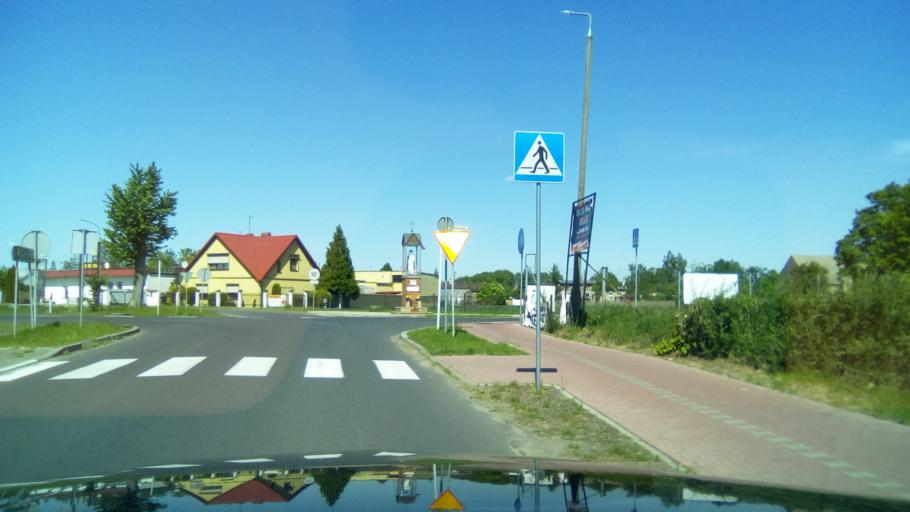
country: PL
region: Greater Poland Voivodeship
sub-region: Powiat gnieznienski
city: Niechanowo
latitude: 52.4701
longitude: 17.6849
